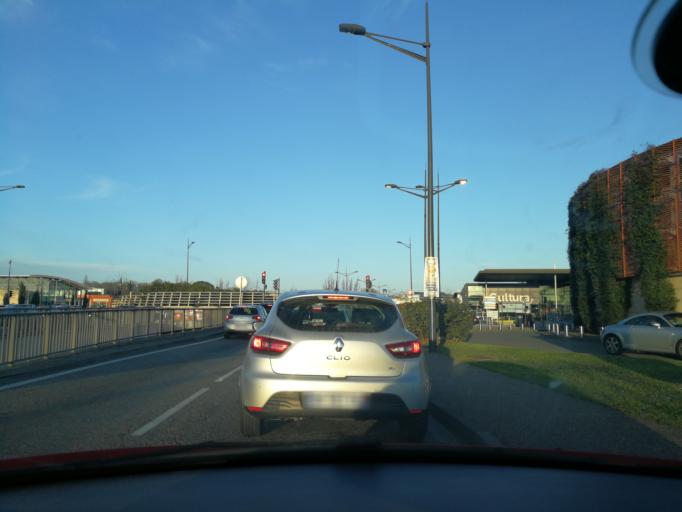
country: FR
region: Midi-Pyrenees
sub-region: Departement de la Haute-Garonne
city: Balma
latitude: 43.6291
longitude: 1.4818
